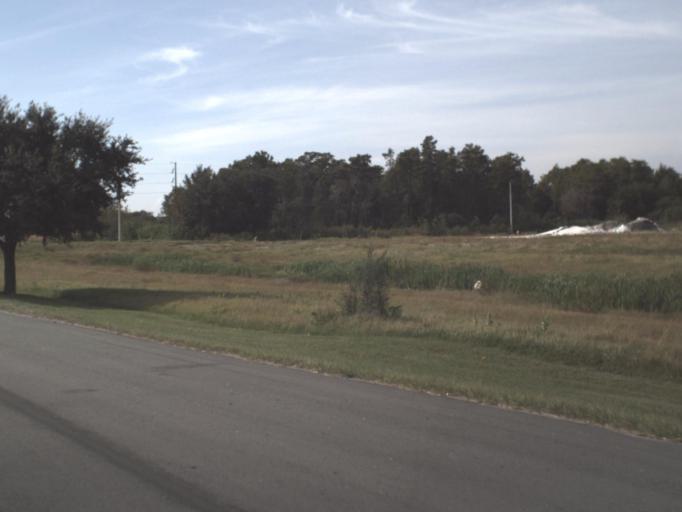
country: US
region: Florida
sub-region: Orange County
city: Williamsburg
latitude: 28.4155
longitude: -81.4230
